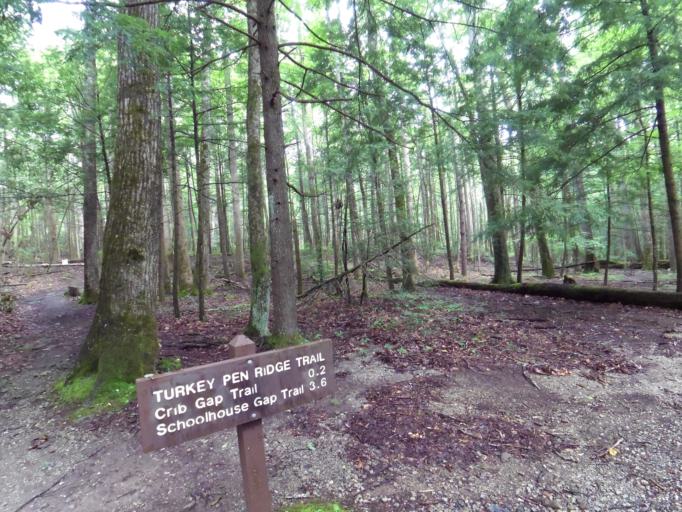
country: US
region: Tennessee
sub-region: Blount County
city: Wildwood
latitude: 35.6067
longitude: -83.7452
